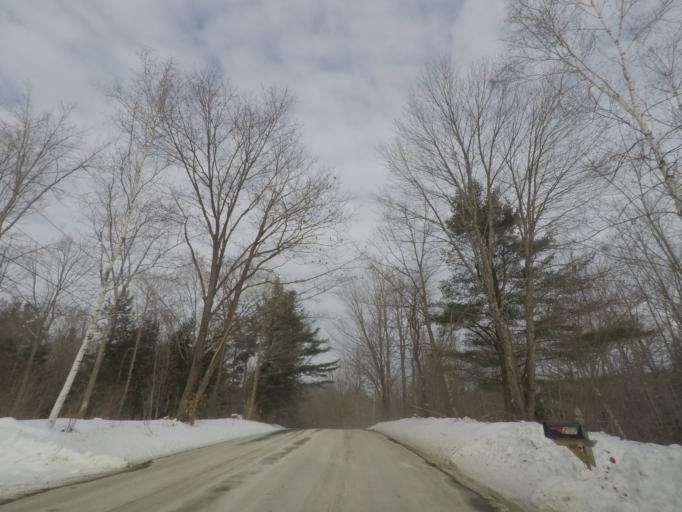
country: US
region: New York
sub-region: Rensselaer County
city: Averill Park
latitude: 42.6032
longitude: -73.4813
